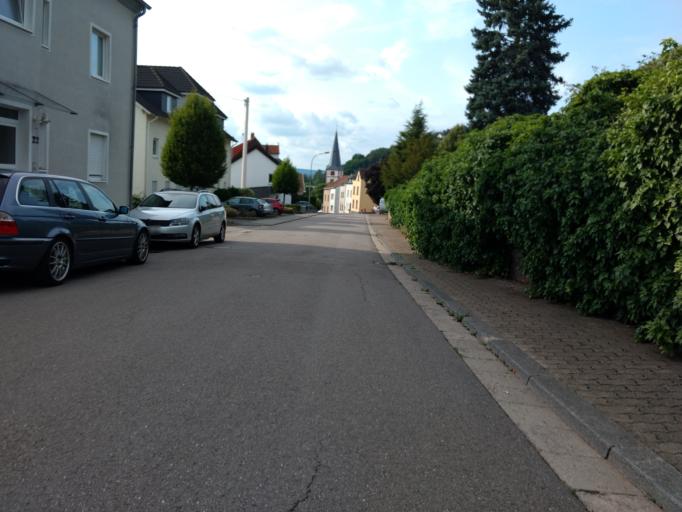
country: DE
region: Saarland
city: Merzig
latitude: 49.4413
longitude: 6.6438
